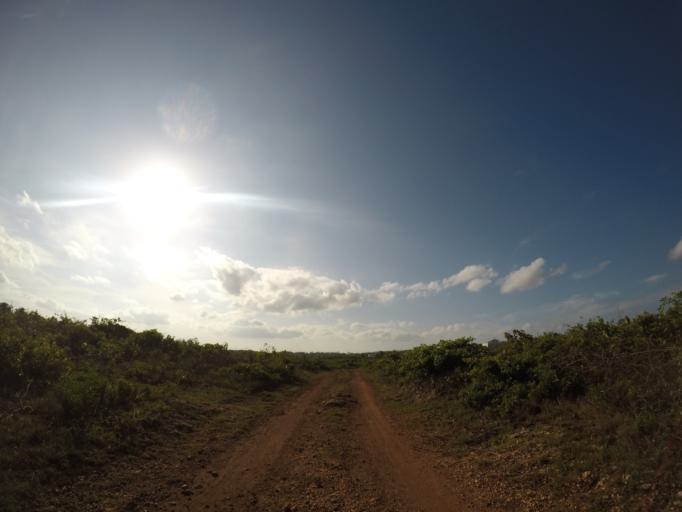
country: TZ
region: Zanzibar Central/South
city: Koani
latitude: -6.2034
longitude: 39.3103
